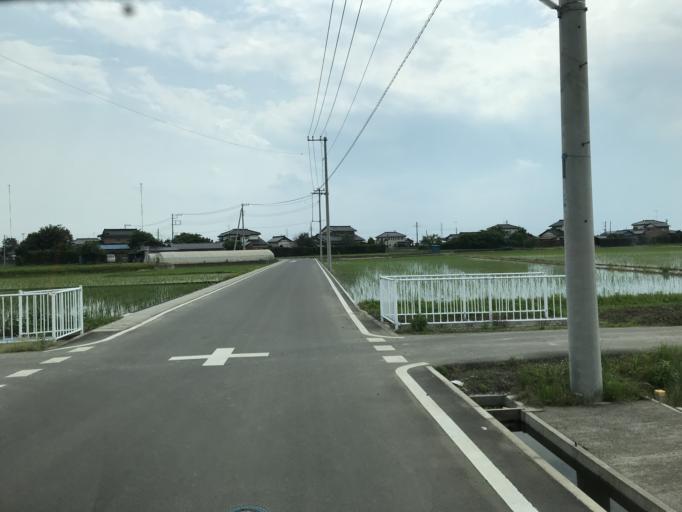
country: JP
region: Saitama
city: Shobu
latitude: 36.0878
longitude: 139.6260
